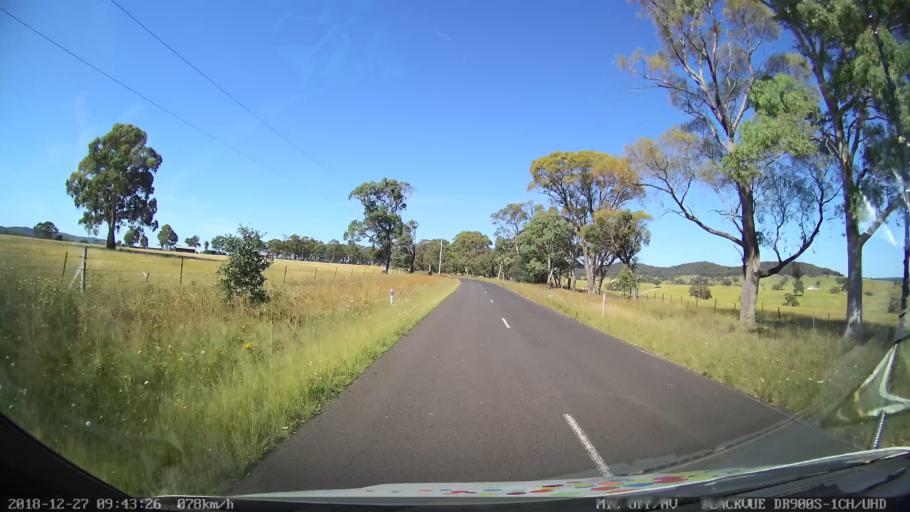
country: AU
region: New South Wales
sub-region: Lithgow
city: Portland
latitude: -33.3062
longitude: 150.0012
